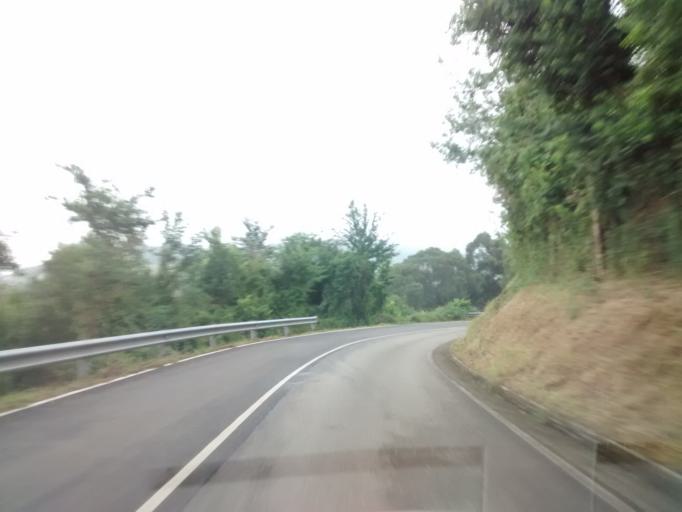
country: ES
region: Asturias
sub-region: Province of Asturias
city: Villaviciosa
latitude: 43.5312
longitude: -5.3908
